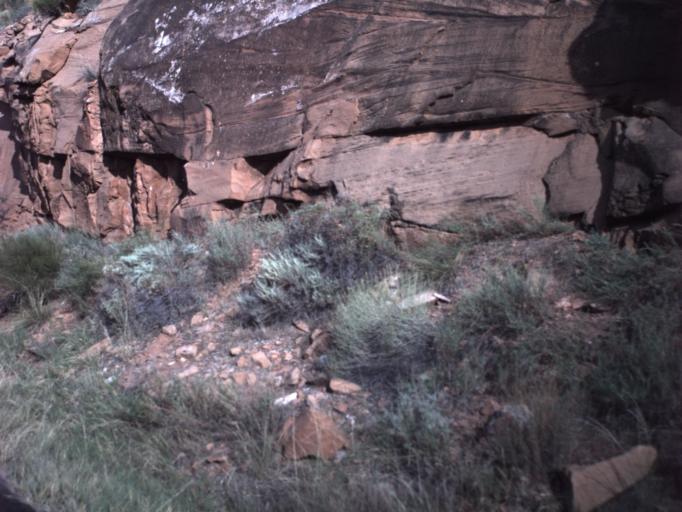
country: US
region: Utah
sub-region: Grand County
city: Moab
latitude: 38.6179
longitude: -109.5240
